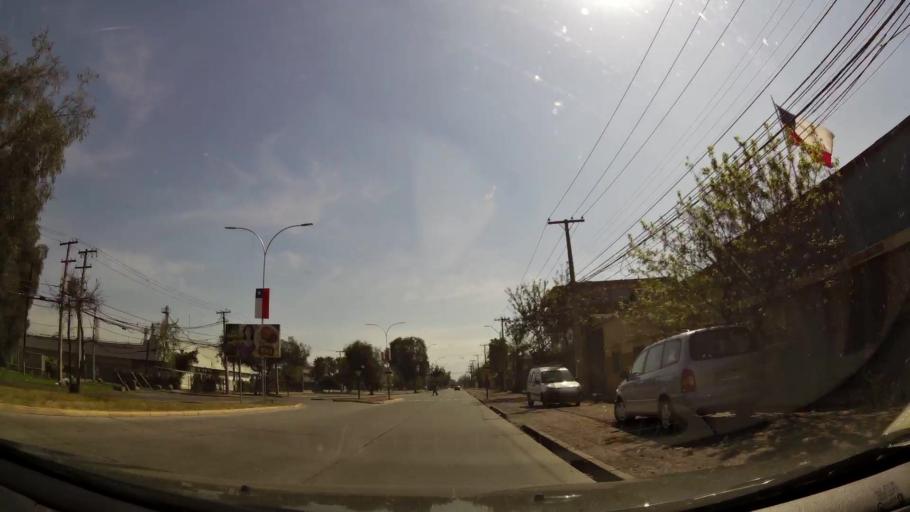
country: CL
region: Santiago Metropolitan
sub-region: Provincia de Santiago
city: Santiago
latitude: -33.4187
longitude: -70.6812
